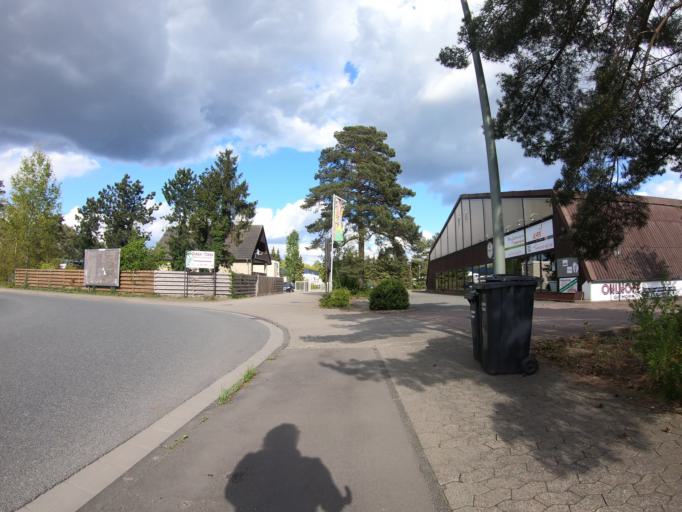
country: DE
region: Lower Saxony
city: Gifhorn
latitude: 52.4645
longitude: 10.5303
